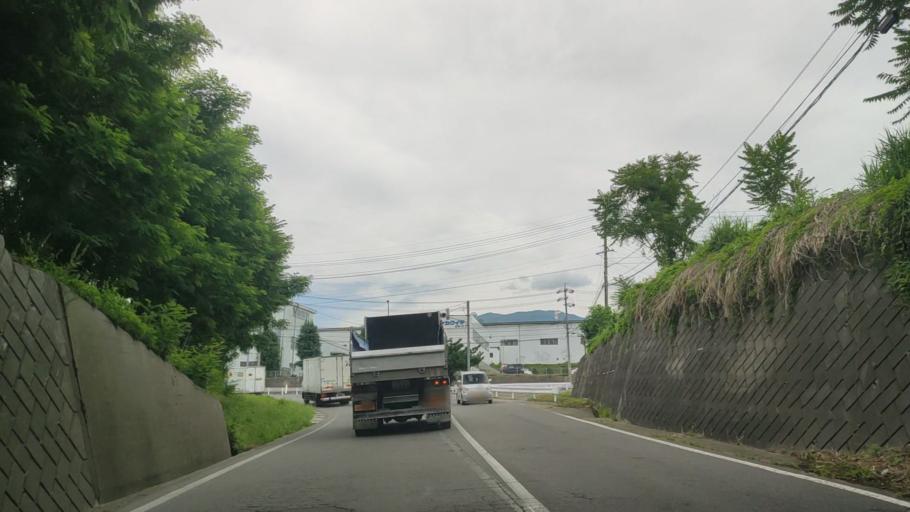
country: JP
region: Nagano
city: Kamimaruko
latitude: 36.3438
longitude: 138.3523
